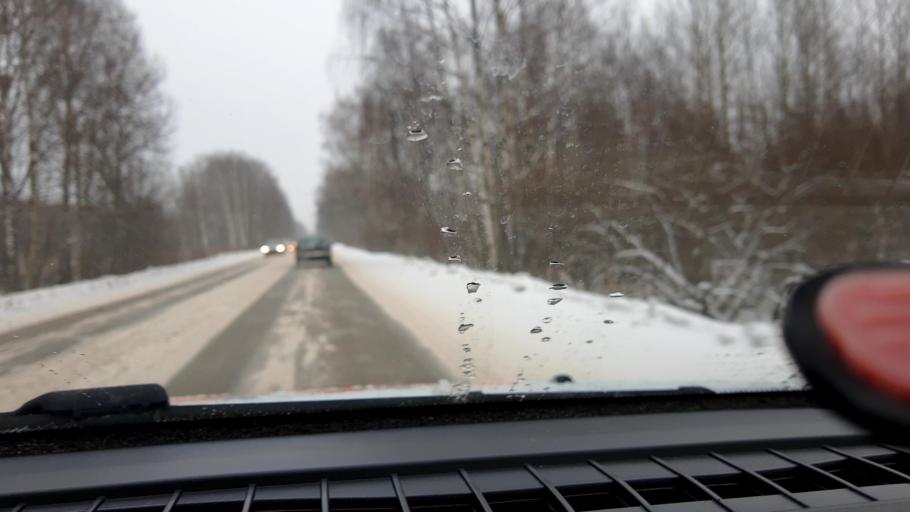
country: RU
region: Nizjnij Novgorod
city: Afonino
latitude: 56.3182
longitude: 44.1818
